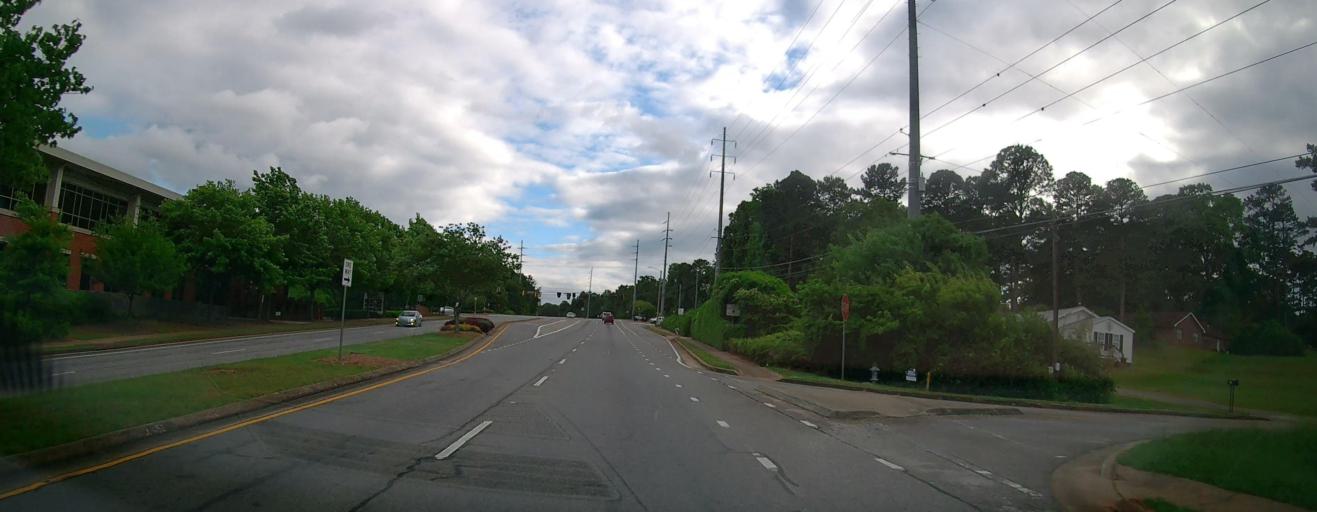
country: US
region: Georgia
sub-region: Clarke County
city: Country Club Estates
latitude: 33.9354
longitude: -83.4365
